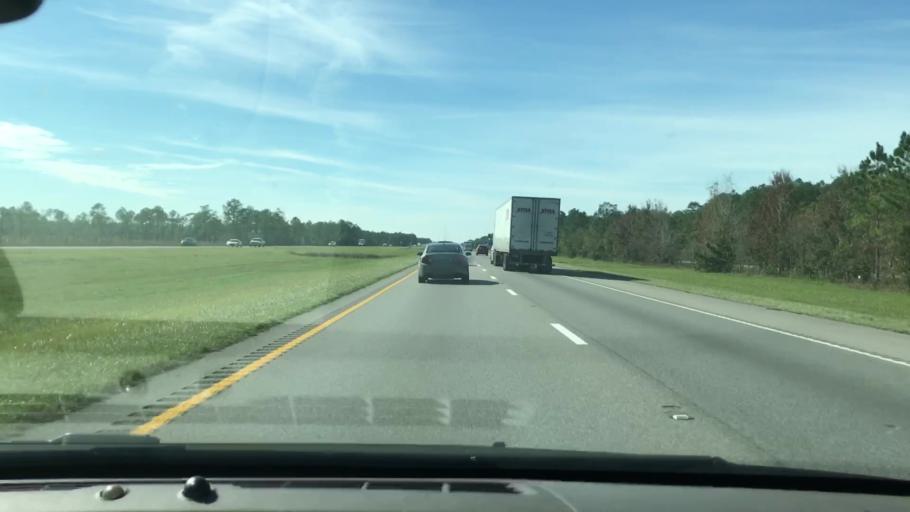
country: US
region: Mississippi
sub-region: Jackson County
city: Hickory Hills
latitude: 30.4371
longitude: -88.6364
